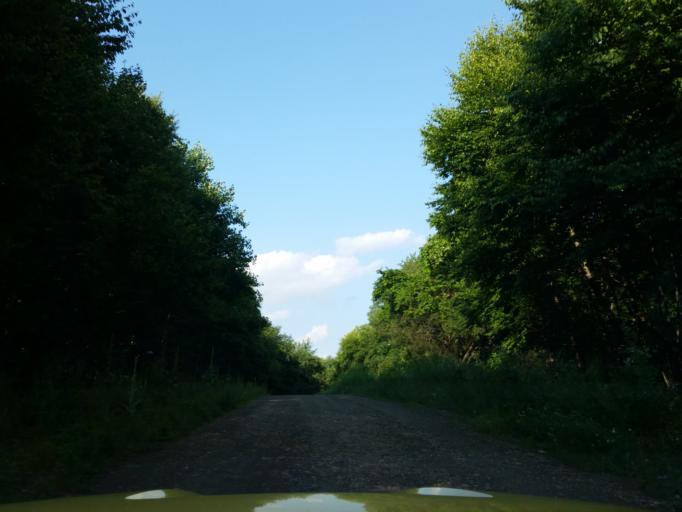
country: US
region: Pennsylvania
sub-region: Dauphin County
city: Williamstown
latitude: 40.4661
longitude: -76.6290
